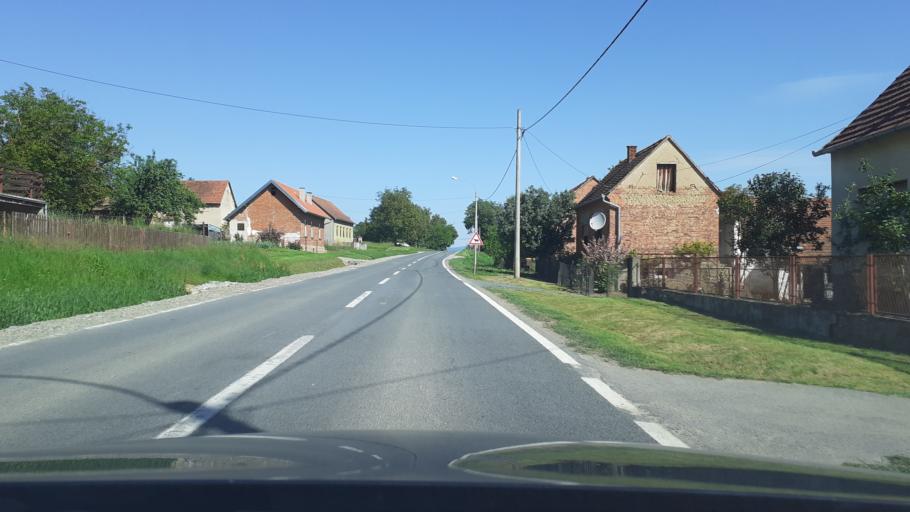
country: HR
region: Pozesko-Slavonska
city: Gradac
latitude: 45.3149
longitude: 17.7769
